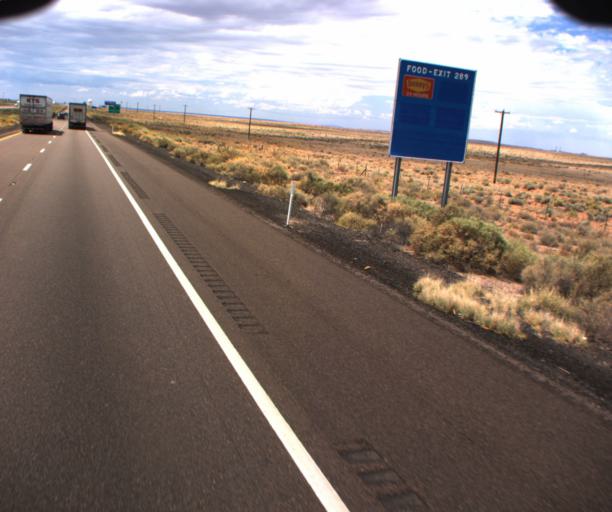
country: US
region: Arizona
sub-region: Navajo County
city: Holbrook
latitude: 34.9492
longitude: -110.1193
